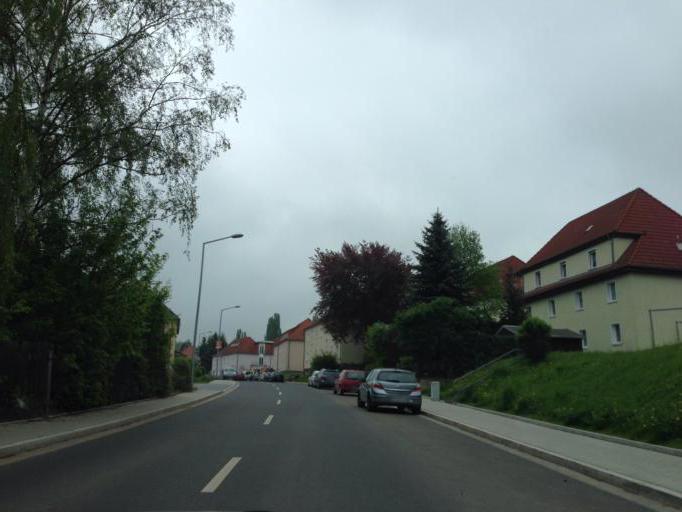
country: DE
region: Saxony
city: Freital
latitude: 51.0133
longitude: 13.6739
